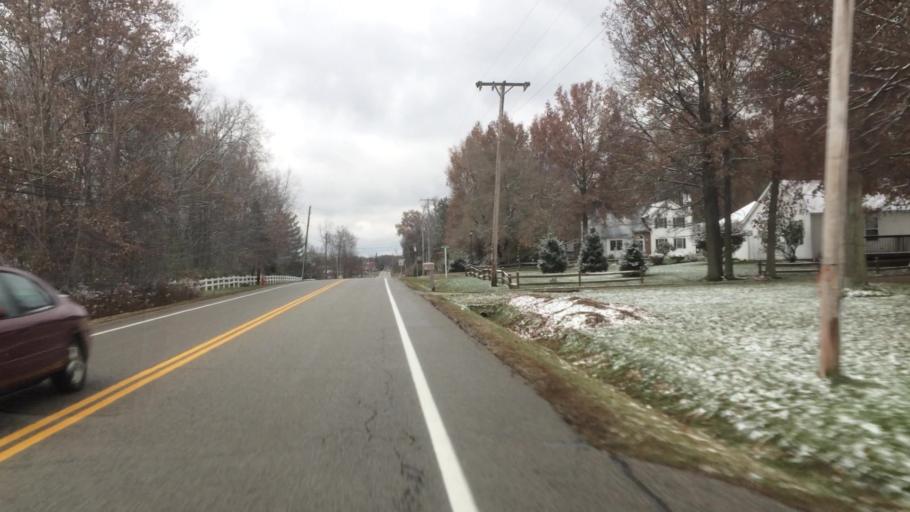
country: US
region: Ohio
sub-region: Summit County
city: Macedonia
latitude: 41.3066
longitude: -81.5328
